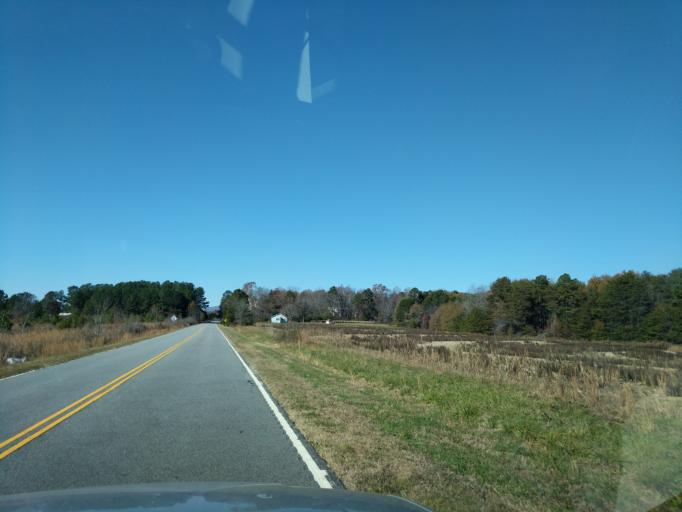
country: US
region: South Carolina
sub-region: Spartanburg County
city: Inman Mills
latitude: 35.0747
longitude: -82.1975
